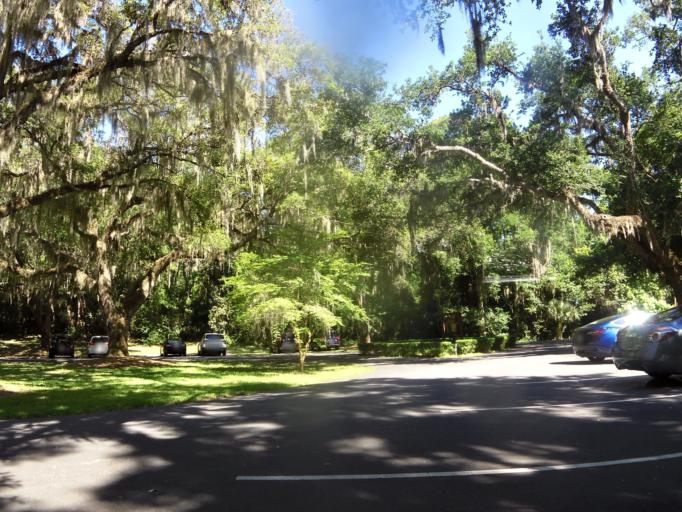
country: US
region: Florida
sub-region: Duval County
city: Atlantic Beach
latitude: 30.3855
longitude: -81.4977
